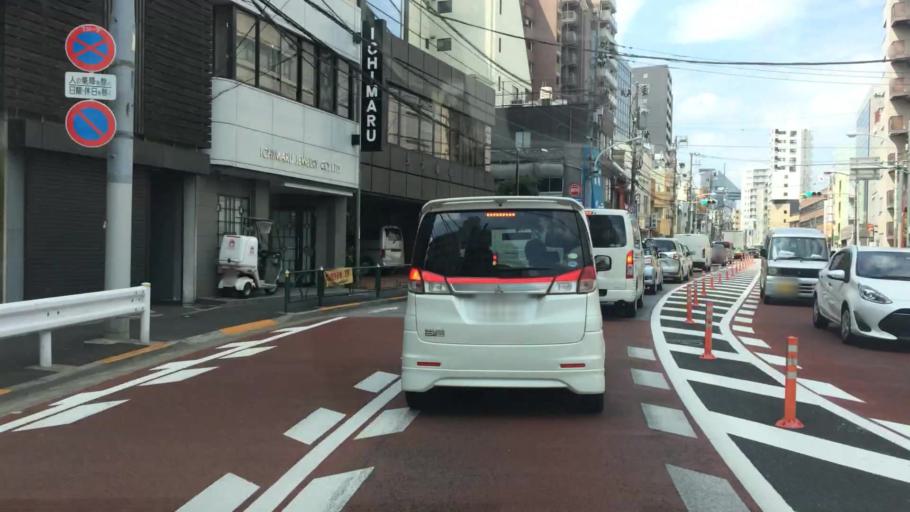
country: JP
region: Tokyo
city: Tokyo
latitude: 35.7073
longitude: 139.7660
